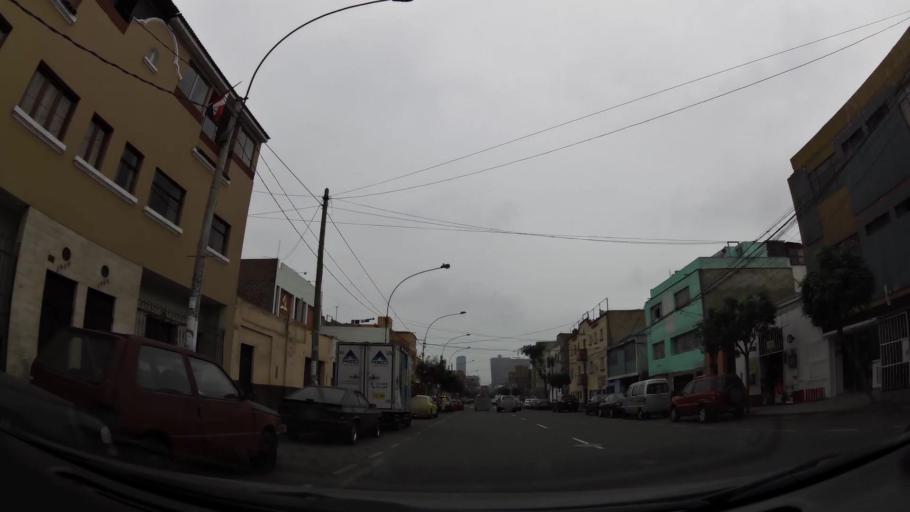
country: PE
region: Lima
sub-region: Lima
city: San Luis
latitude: -12.0831
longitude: -77.0293
